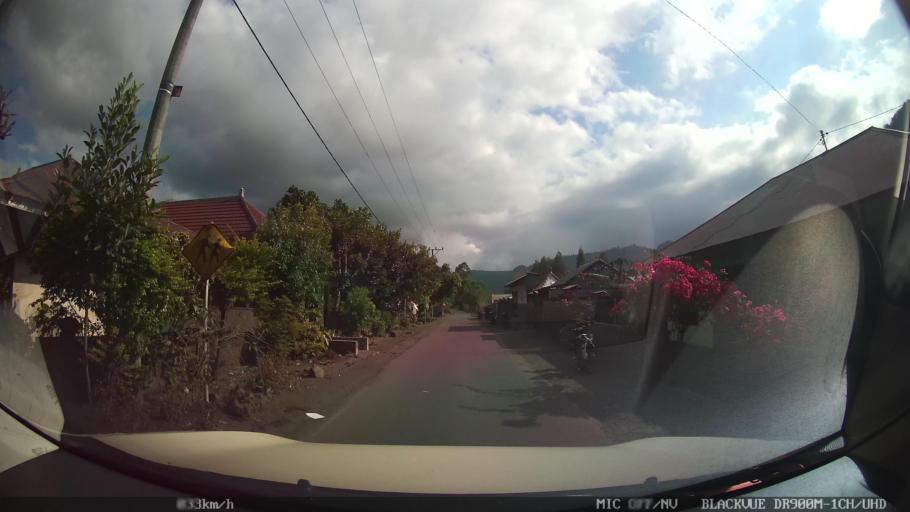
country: ID
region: Bali
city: Banjar Kedisan
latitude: -8.2204
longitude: 115.3630
